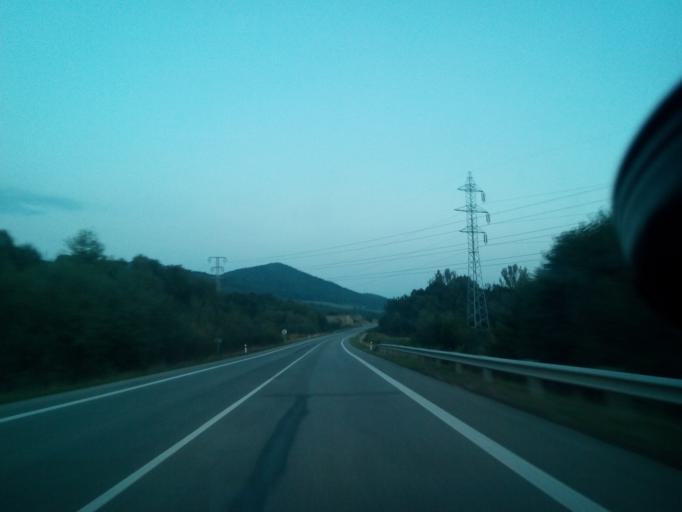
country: SK
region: Kosicky
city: Roznava
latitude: 48.6949
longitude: 20.5129
